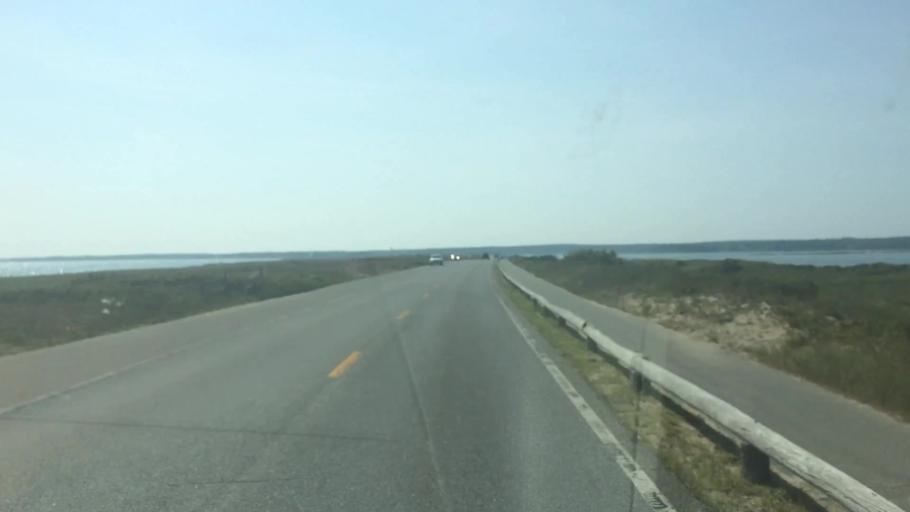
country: US
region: Massachusetts
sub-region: Dukes County
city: Oak Bluffs
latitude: 41.4243
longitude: -70.5540
